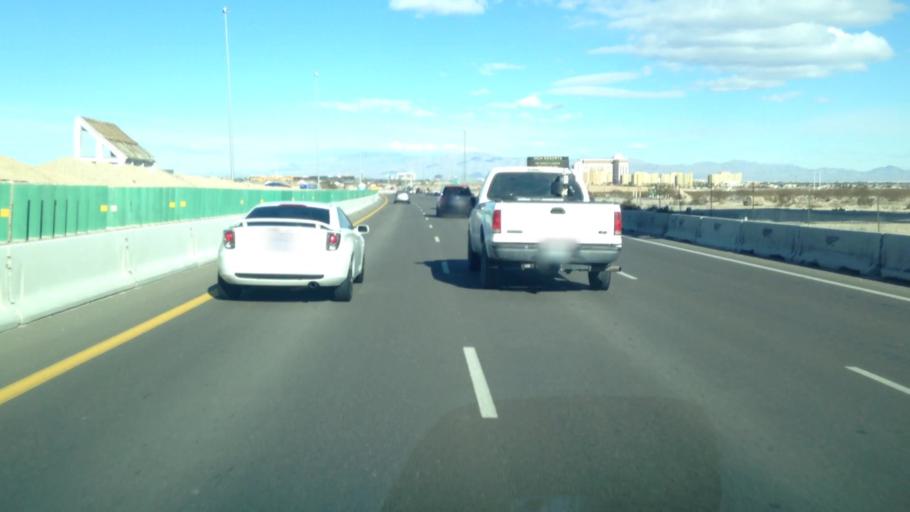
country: US
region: Nevada
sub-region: Clark County
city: Enterprise
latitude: 35.9874
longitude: -115.1805
